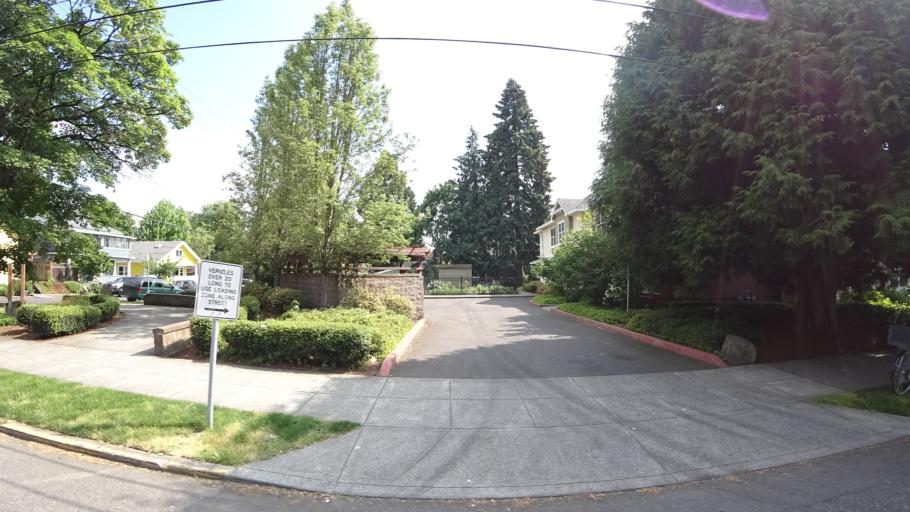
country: US
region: Oregon
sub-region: Multnomah County
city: Portland
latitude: 45.5193
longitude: -122.6312
